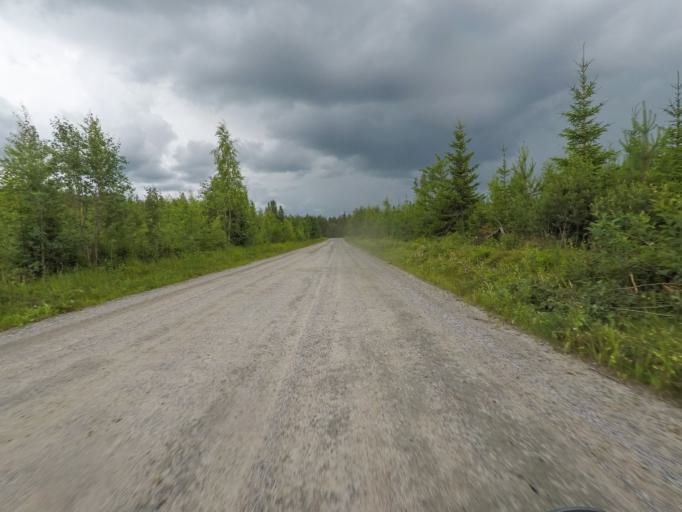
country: FI
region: Central Finland
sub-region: Jyvaeskylae
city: Hankasalmi
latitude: 62.4075
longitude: 26.6042
